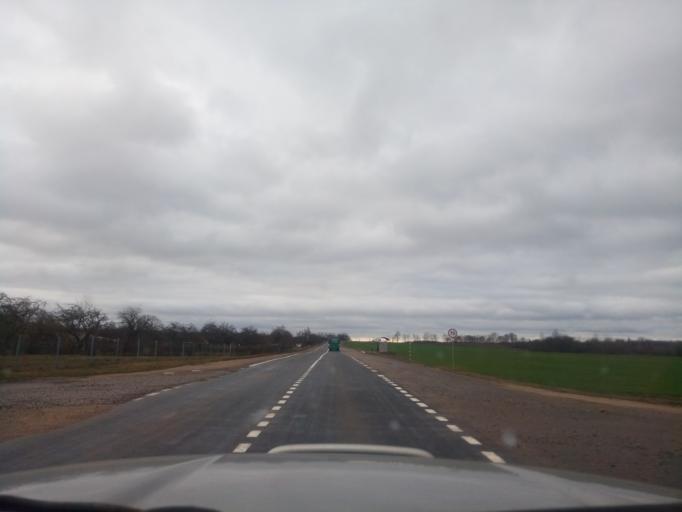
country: BY
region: Minsk
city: Kapyl'
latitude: 53.1761
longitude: 27.1648
